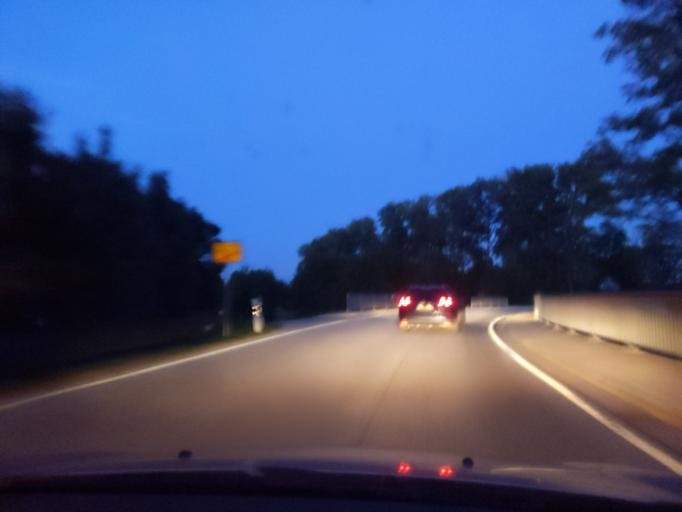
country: DE
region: Saxony
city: Malschwitz
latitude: 51.2617
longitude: 14.5261
